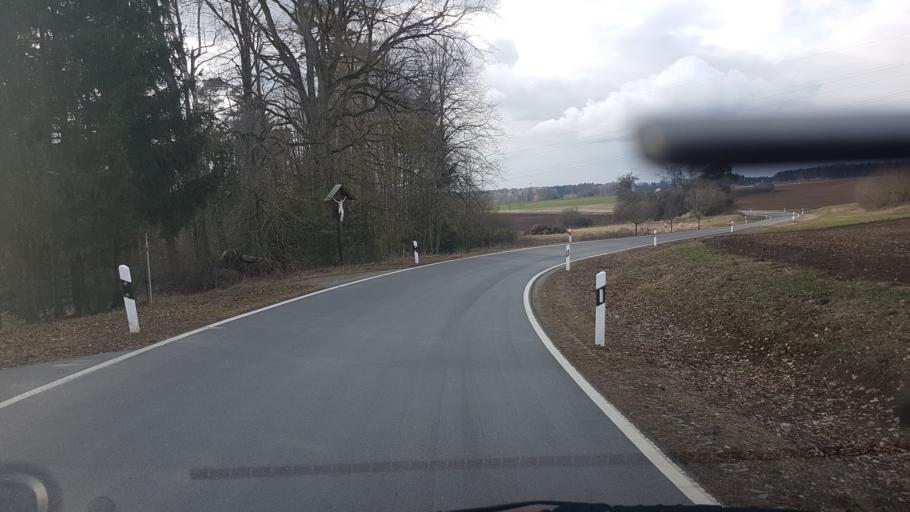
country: DE
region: Bavaria
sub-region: Upper Franconia
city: Stadelhofen
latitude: 50.0039
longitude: 11.1924
